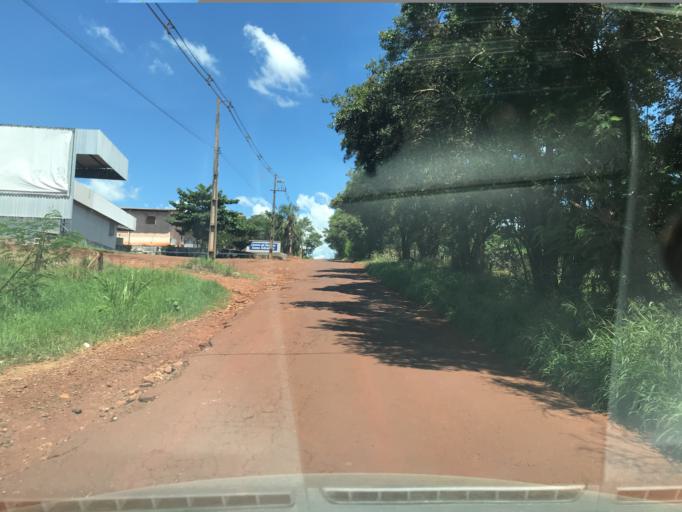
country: BR
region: Parana
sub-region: Palotina
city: Palotina
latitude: -24.2936
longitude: -53.8535
